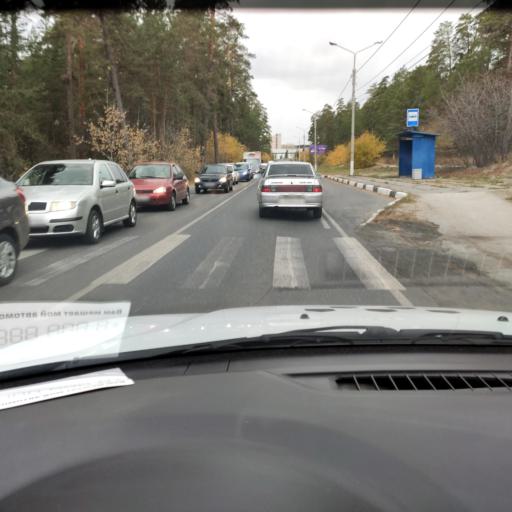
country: RU
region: Samara
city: Tol'yatti
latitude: 53.4762
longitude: 49.3328
